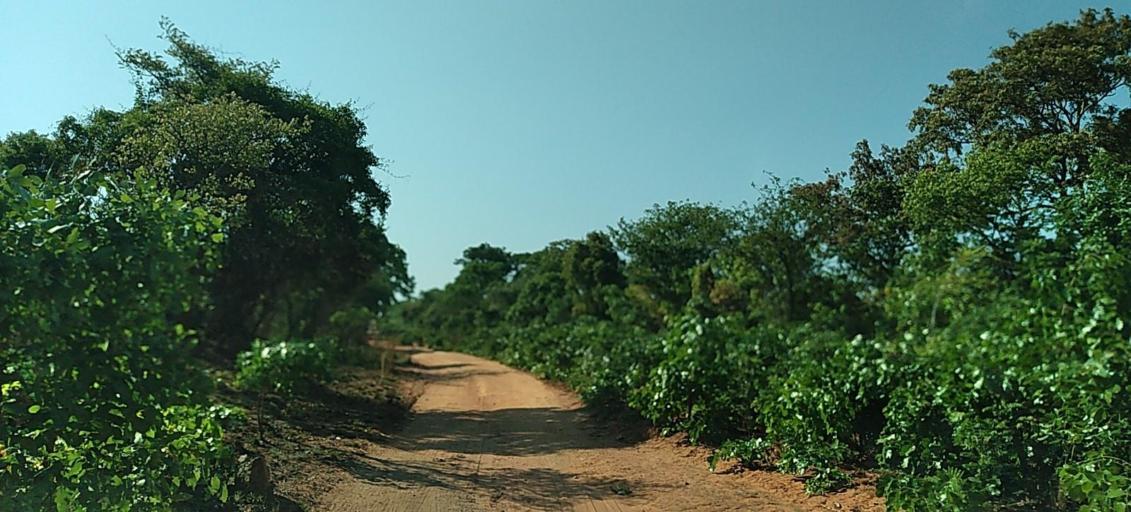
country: ZM
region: Central
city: Mkushi
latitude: -13.4711
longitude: 28.9175
